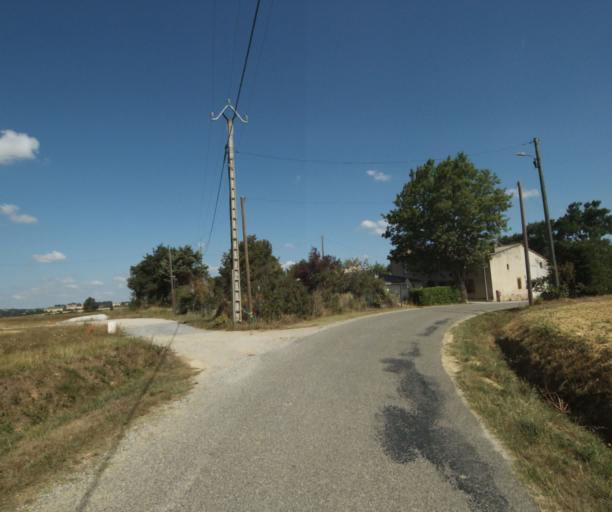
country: FR
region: Midi-Pyrenees
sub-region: Departement de la Haute-Garonne
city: Auriac-sur-Vendinelle
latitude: 43.4512
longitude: 1.7894
